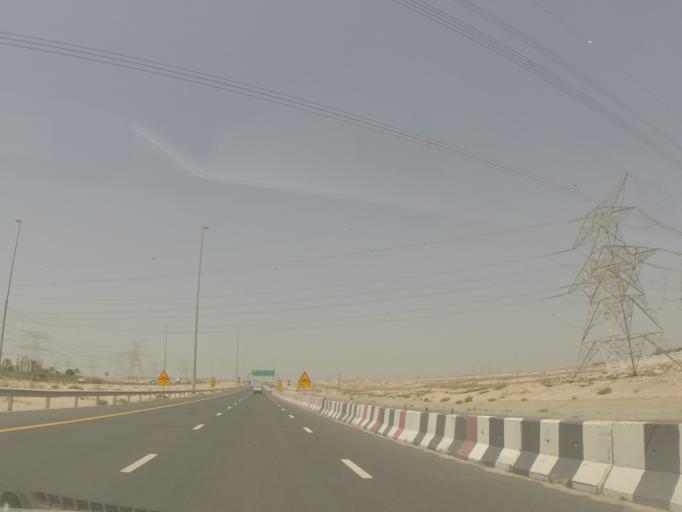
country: AE
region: Dubai
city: Dubai
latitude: 25.0093
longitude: 55.1687
